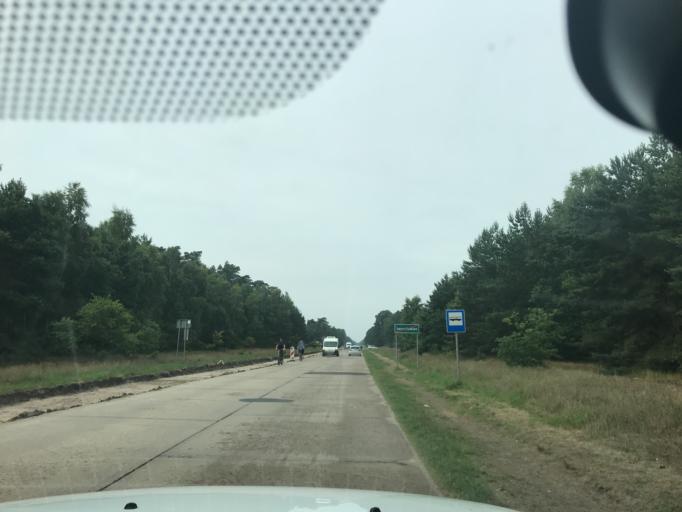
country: PL
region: West Pomeranian Voivodeship
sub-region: Powiat slawienski
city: Darlowo
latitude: 54.5300
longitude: 16.5193
